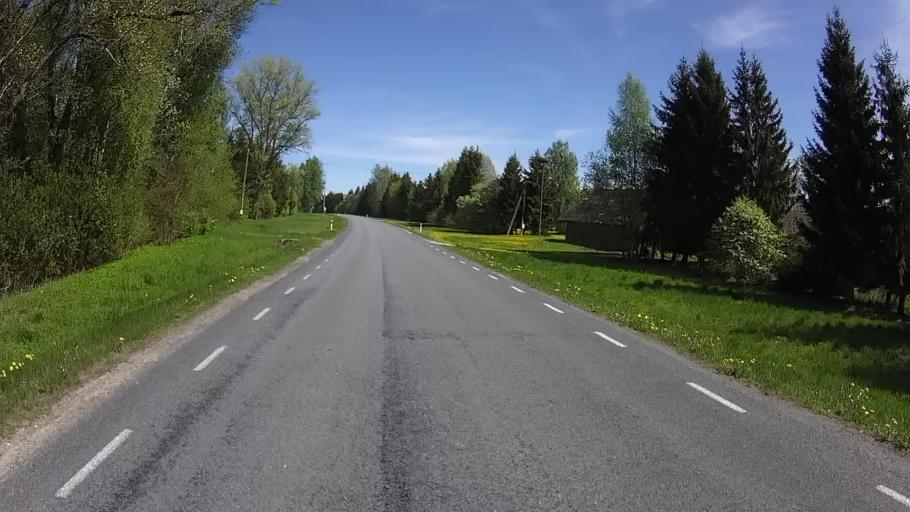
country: LV
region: Apes Novads
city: Ape
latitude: 57.6073
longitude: 26.5641
